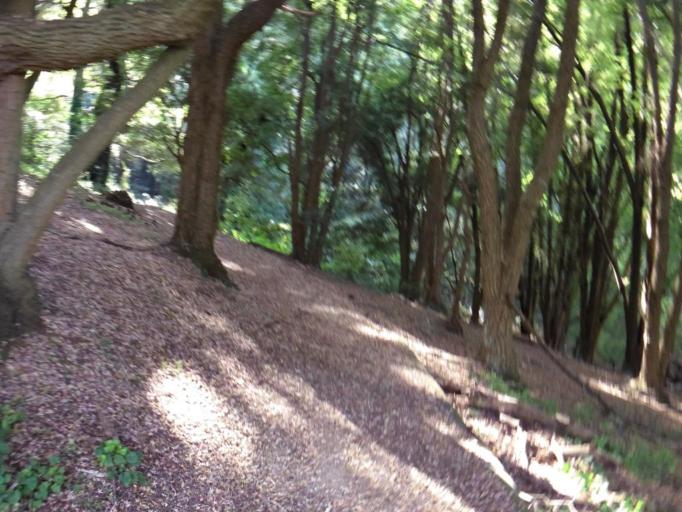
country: AU
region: Victoria
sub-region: Yarra Ranges
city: Kalorama
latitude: -37.8188
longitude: 145.3688
